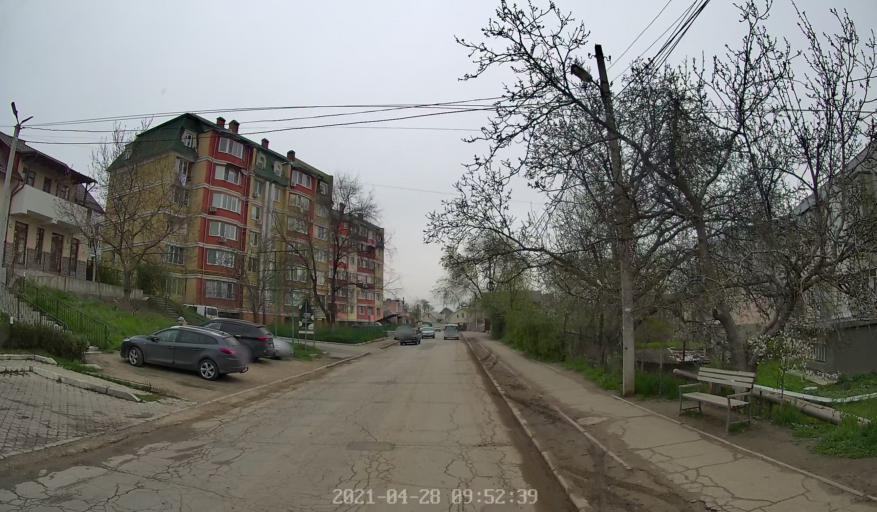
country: MD
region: Chisinau
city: Singera
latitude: 46.9825
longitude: 28.9335
